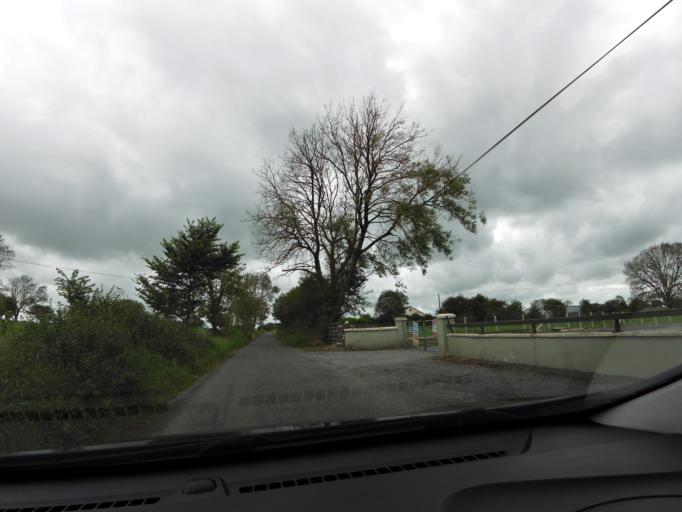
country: IE
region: Connaught
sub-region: County Galway
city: Athenry
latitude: 53.3237
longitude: -8.7315
